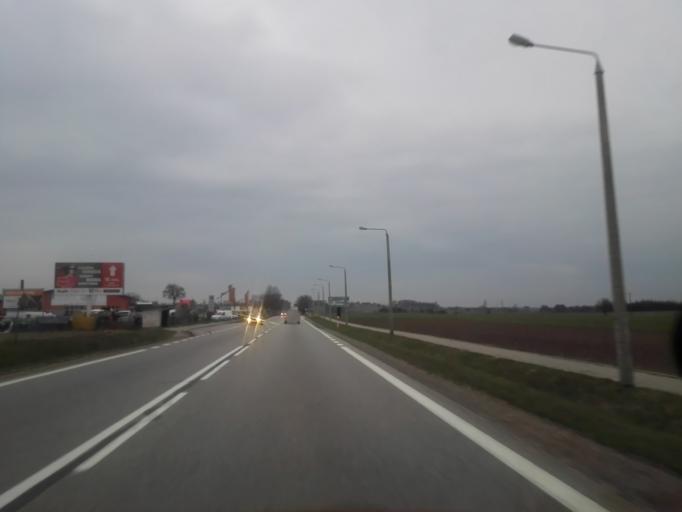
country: PL
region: Podlasie
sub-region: Powiat lomzynski
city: Piatnica
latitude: 53.2446
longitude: 22.1180
